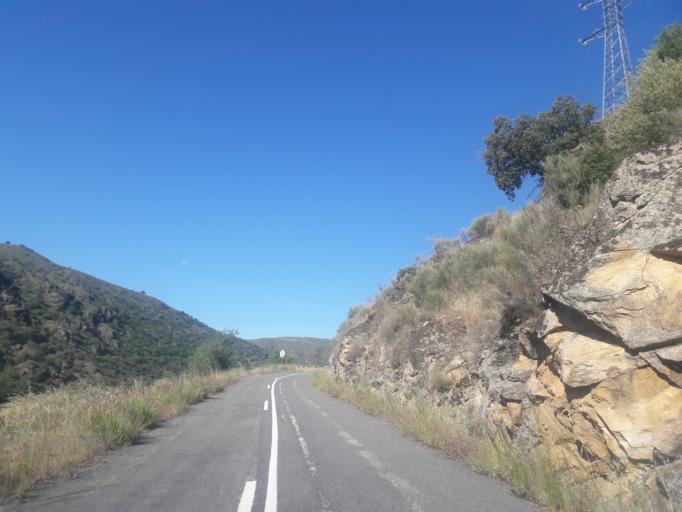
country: ES
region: Castille and Leon
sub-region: Provincia de Salamanca
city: Saucelle
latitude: 41.0289
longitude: -6.7371
